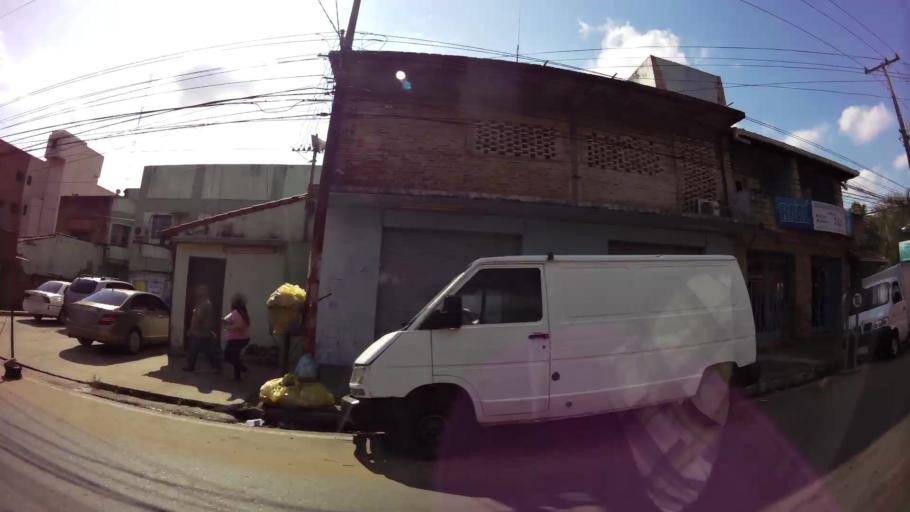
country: PY
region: Central
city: Fernando de la Mora
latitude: -25.3265
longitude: -57.5452
